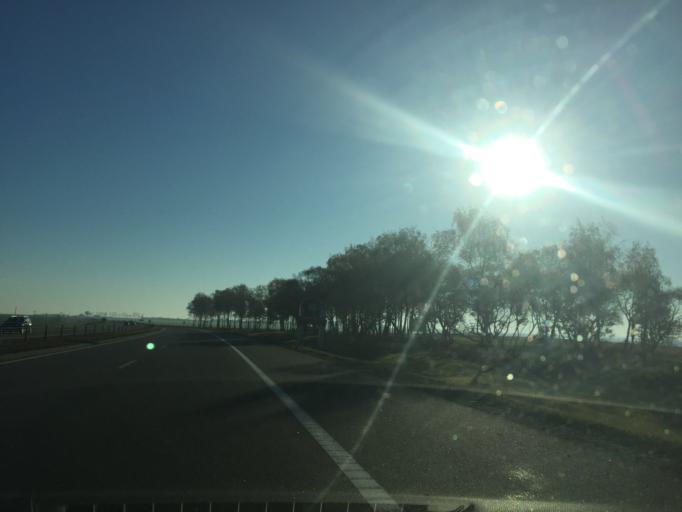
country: BY
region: Minsk
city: Luhavaya Slabada
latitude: 53.7619
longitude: 27.8801
